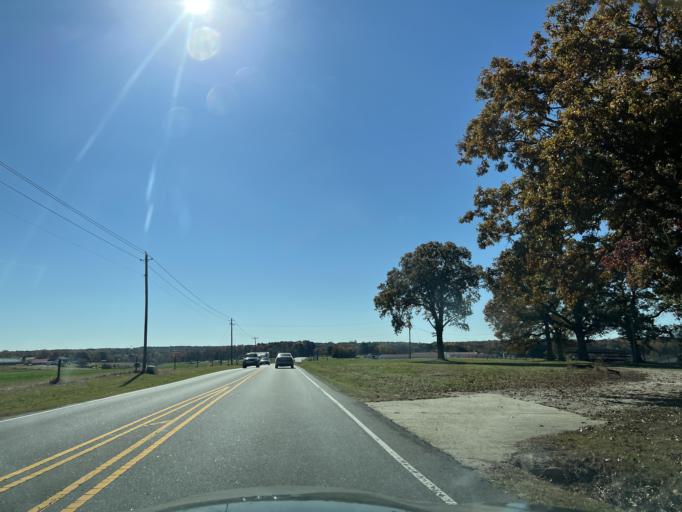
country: US
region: North Carolina
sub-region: Wake County
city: West Raleigh
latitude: 35.7299
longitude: -78.6830
